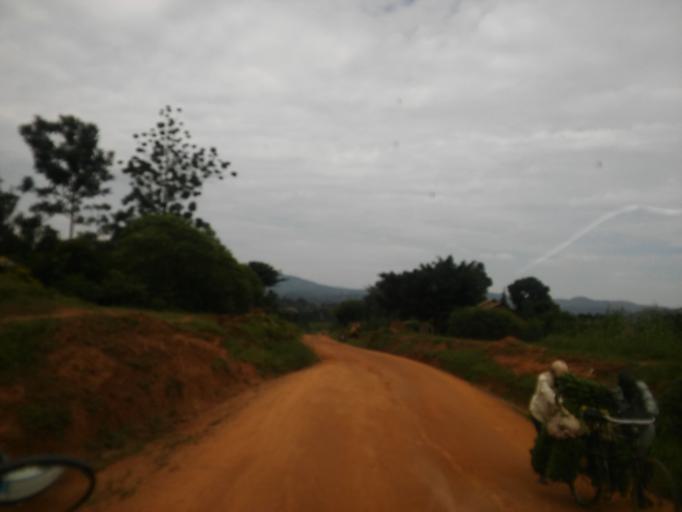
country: UG
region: Eastern Region
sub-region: Mbale District
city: Mbale
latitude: 0.9666
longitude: 34.2094
